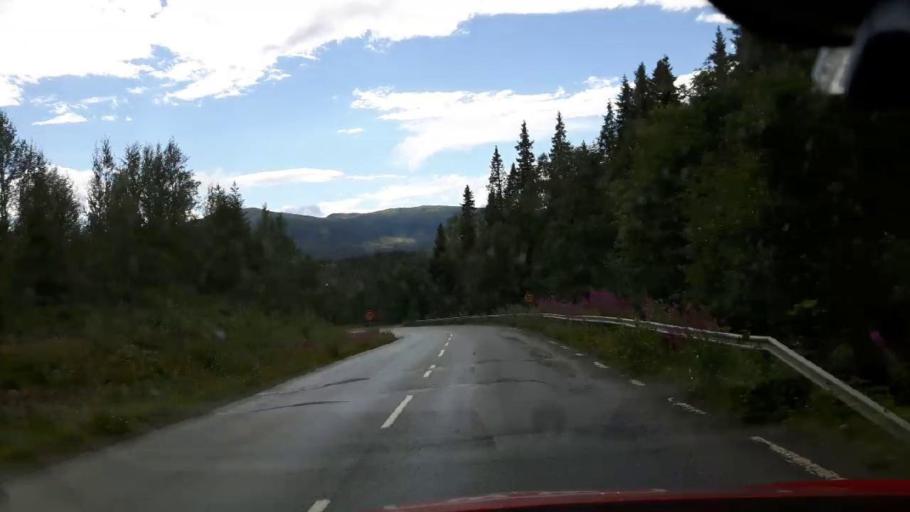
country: SE
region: Jaemtland
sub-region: Are Kommun
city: Are
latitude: 63.3195
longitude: 13.2324
